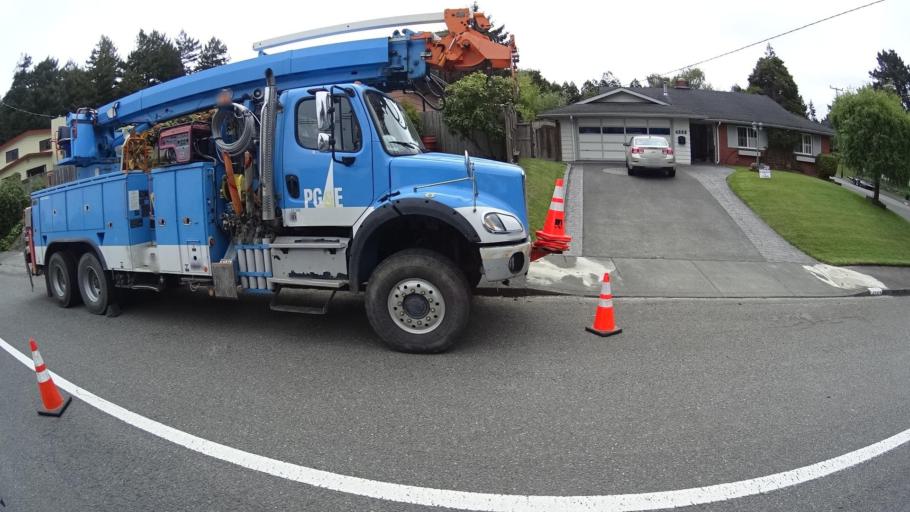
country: US
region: California
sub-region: Humboldt County
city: Bayview
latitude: 40.7643
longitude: -124.1643
